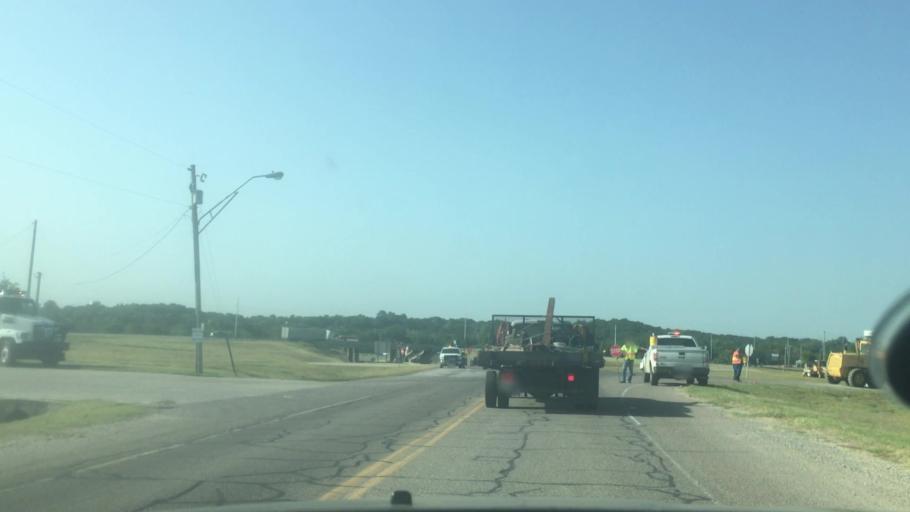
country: US
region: Oklahoma
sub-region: Bryan County
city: Durant
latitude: 34.0230
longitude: -96.3904
